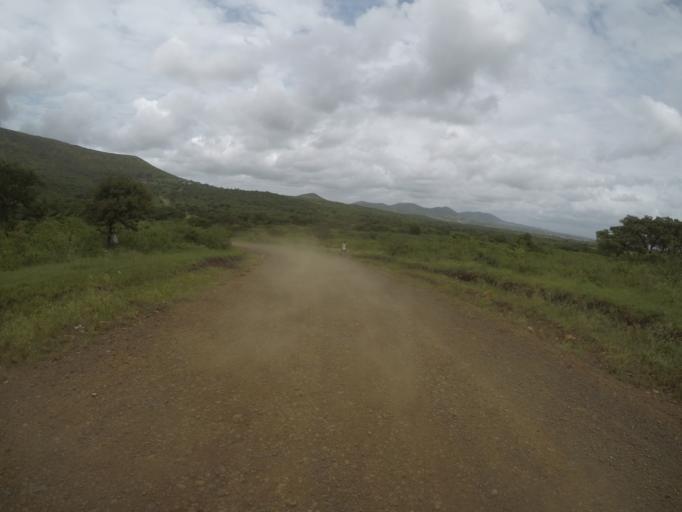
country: ZA
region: KwaZulu-Natal
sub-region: uThungulu District Municipality
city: Empangeni
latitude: -28.5940
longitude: 31.8906
